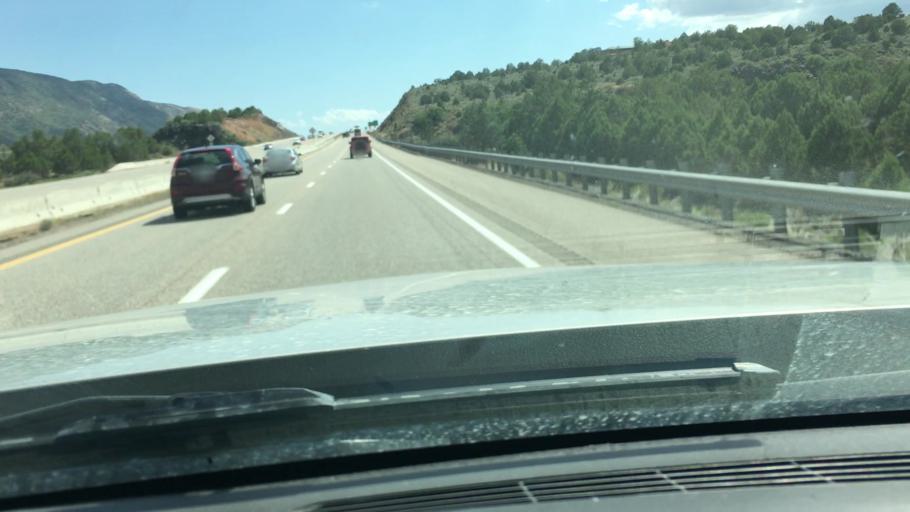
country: US
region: Utah
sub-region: Washington County
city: Toquerville
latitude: 37.4132
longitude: -113.2356
